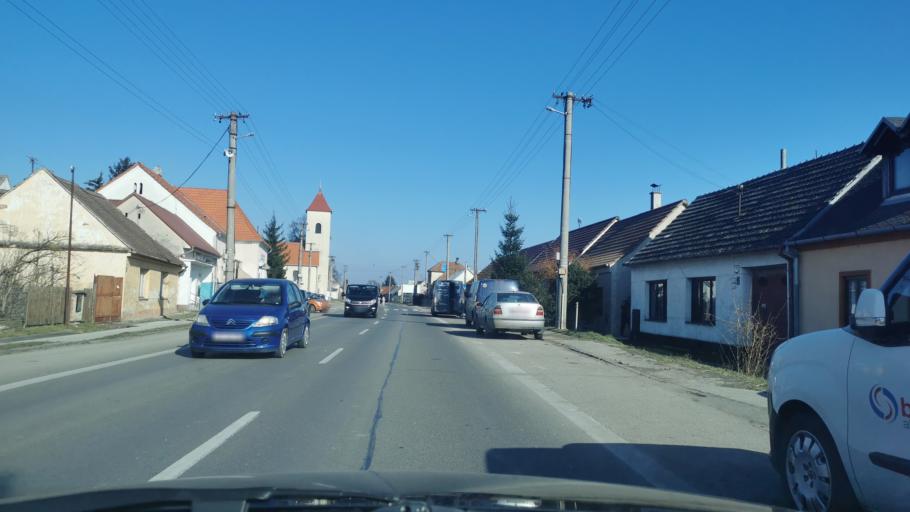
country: SK
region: Trnavsky
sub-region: Okres Senica
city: Senica
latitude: 48.6775
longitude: 17.3372
